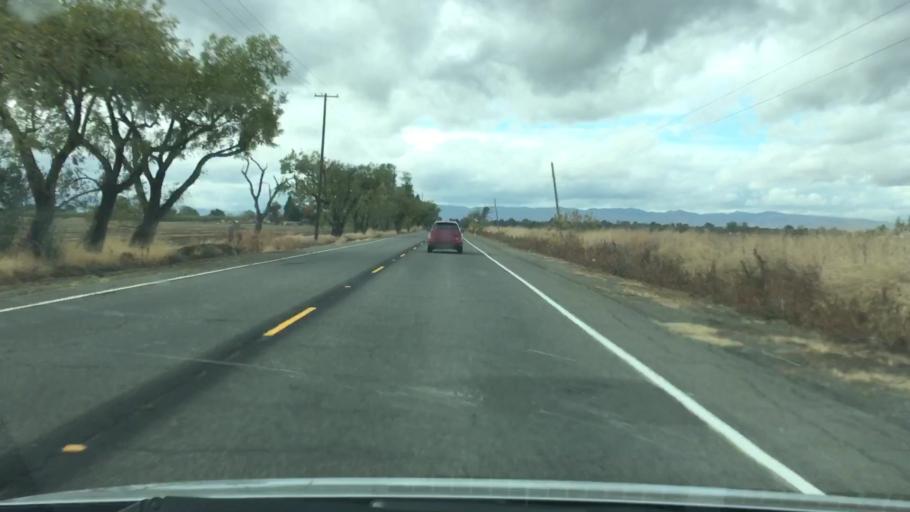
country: US
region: California
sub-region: Yolo County
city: Davis
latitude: 38.5616
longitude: -121.8260
